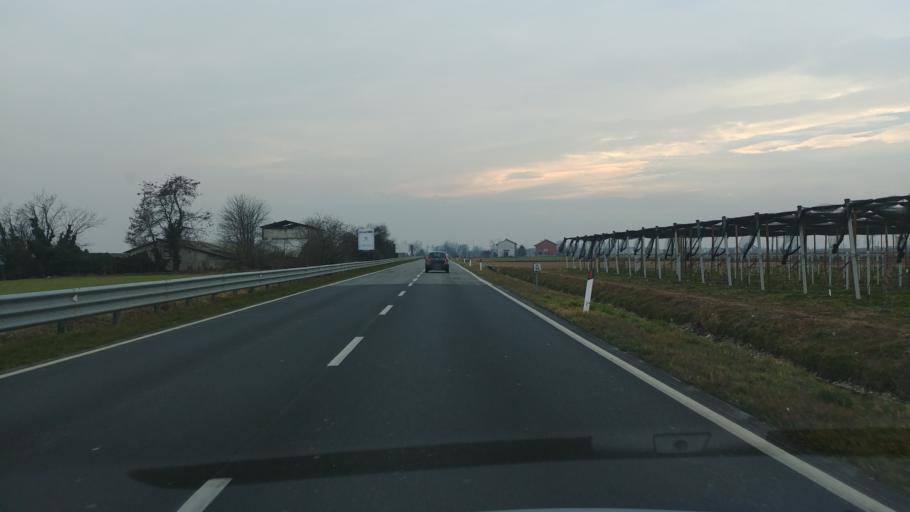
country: IT
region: Piedmont
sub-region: Provincia di Cuneo
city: Montanera
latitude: 44.4992
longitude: 7.6732
